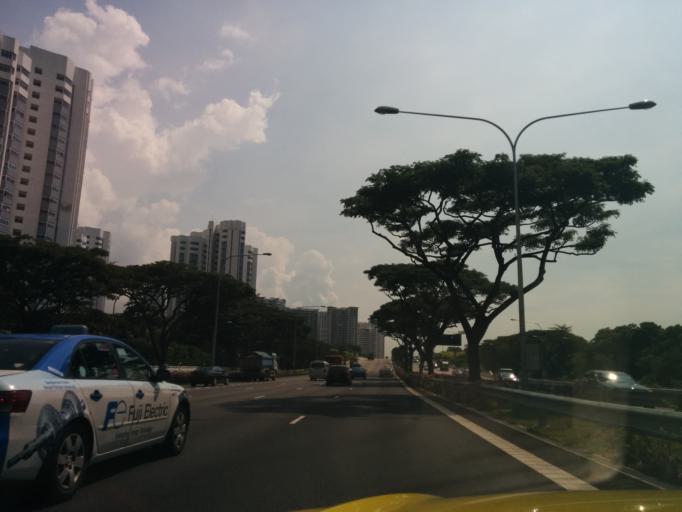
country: SG
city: Singapore
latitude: 1.2957
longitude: 103.8815
